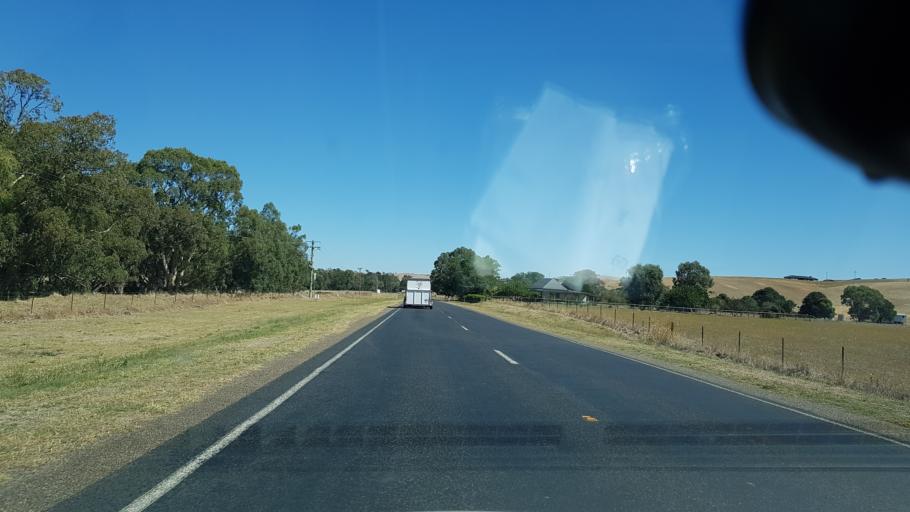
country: AU
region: New South Wales
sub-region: Gundagai
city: Gundagai
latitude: -34.8205
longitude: 148.3539
